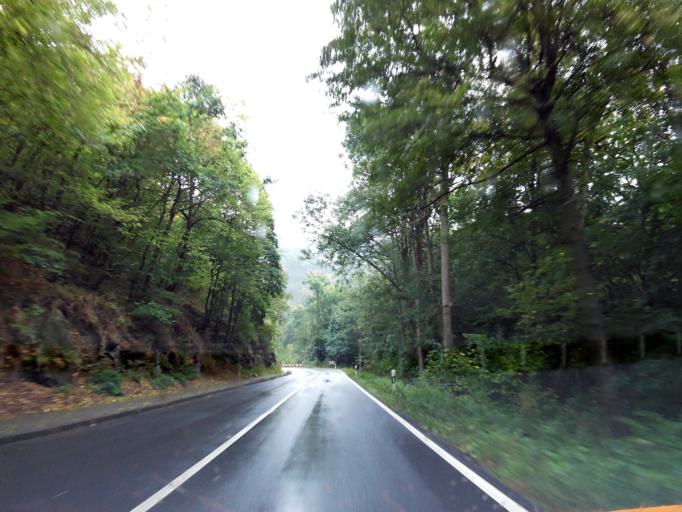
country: DE
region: Saxony-Anhalt
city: Harzgerode
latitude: 51.6671
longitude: 11.1294
